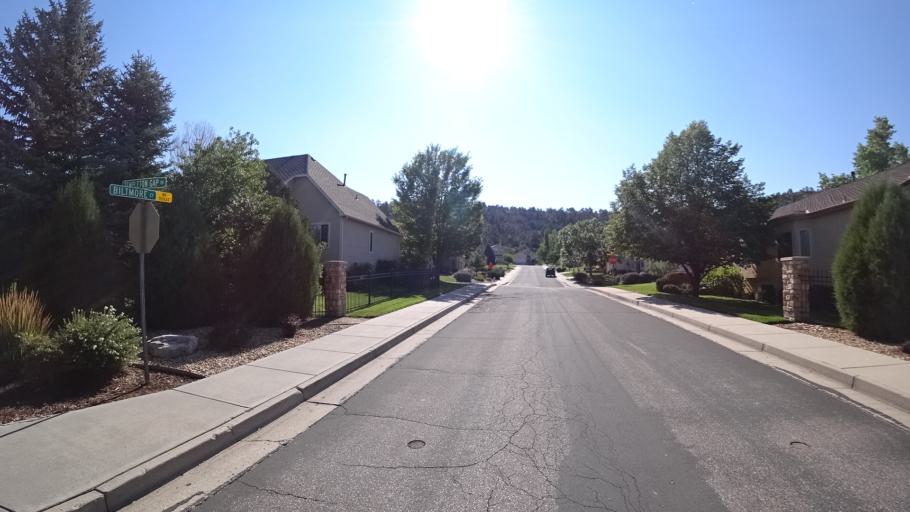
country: US
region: Colorado
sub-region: El Paso County
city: Colorado Springs
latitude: 38.8874
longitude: -104.7840
